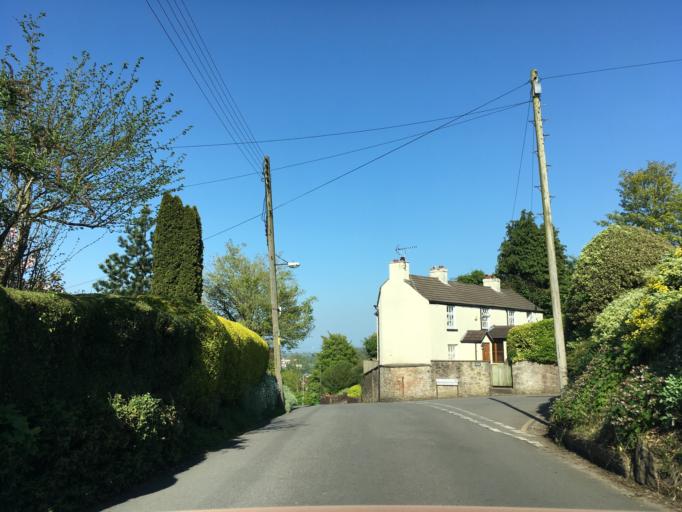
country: GB
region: Wales
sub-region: Monmouthshire
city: Chepstow
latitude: 51.6396
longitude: -2.6823
